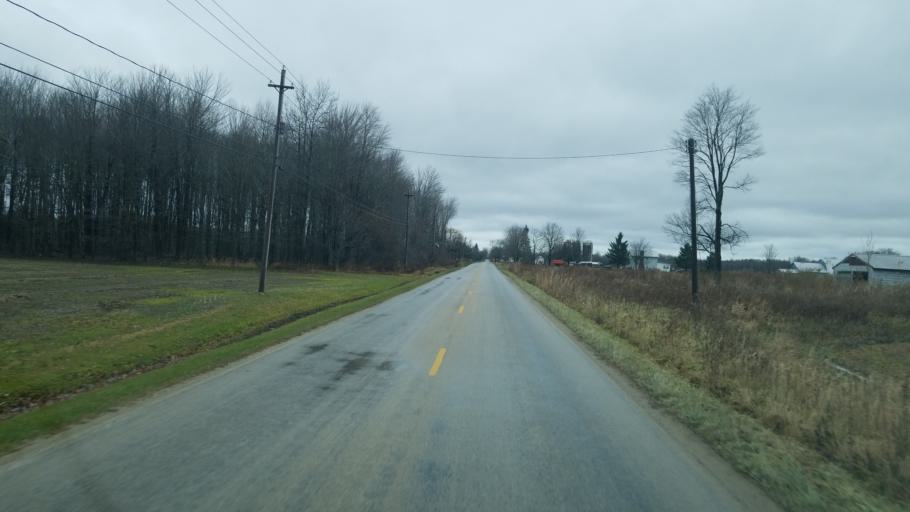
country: US
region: Ohio
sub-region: Ashtabula County
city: North Kingsville
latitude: 41.7754
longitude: -80.6233
